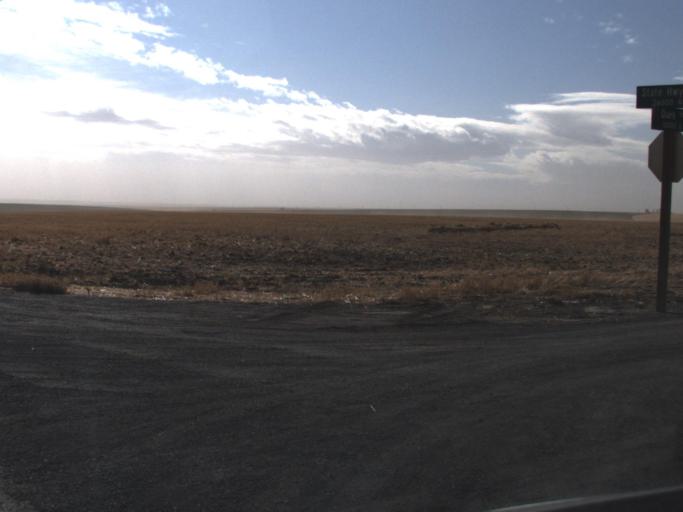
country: US
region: Washington
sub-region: Okanogan County
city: Coulee Dam
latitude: 47.6415
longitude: -118.7210
